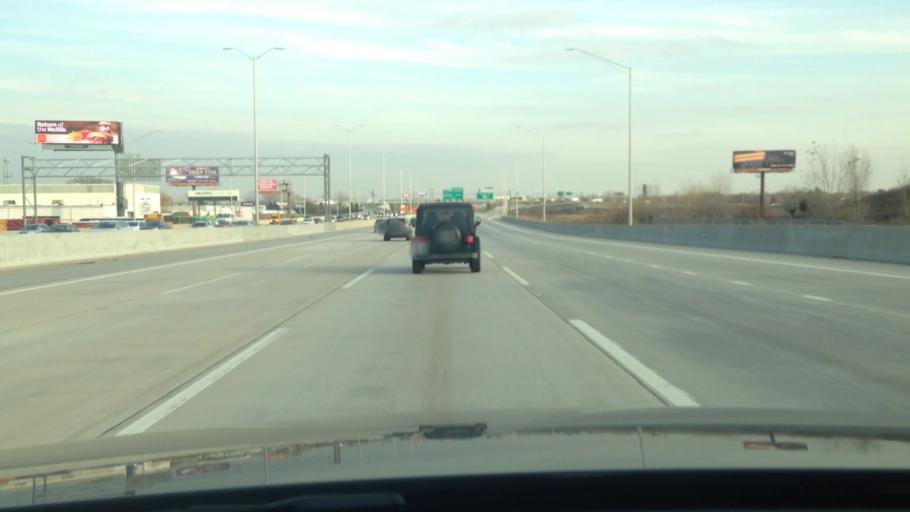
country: US
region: Illinois
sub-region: Cook County
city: Elk Grove Village
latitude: 42.0200
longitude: -87.9505
